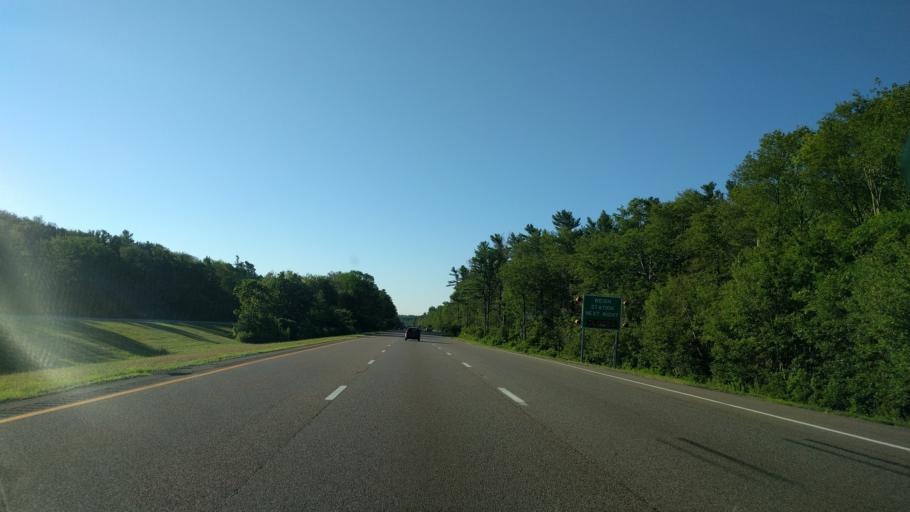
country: US
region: Massachusetts
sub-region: Bristol County
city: Raynham Center
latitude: 41.9369
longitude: -71.0130
